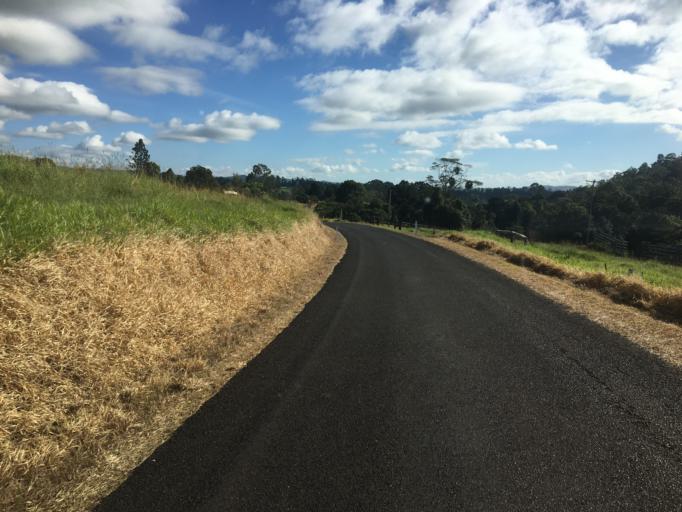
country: AU
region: Queensland
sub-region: Tablelands
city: Ravenshoe
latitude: -17.5760
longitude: 145.6101
